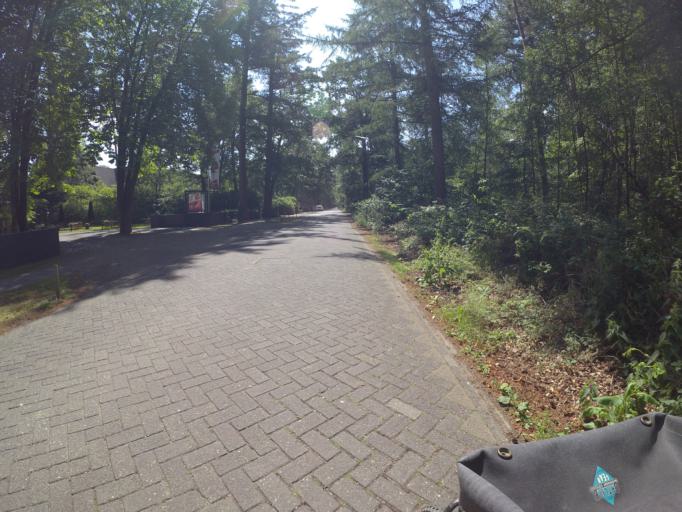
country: NL
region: North Brabant
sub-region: Gemeente Haaren
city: Haaren
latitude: 51.5696
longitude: 5.2319
